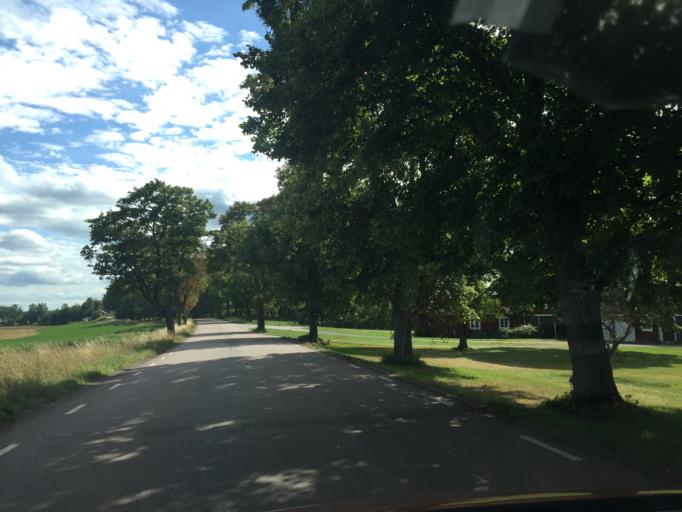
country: SE
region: OErebro
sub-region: Askersunds Kommun
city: Asbro
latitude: 59.0992
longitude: 15.0066
